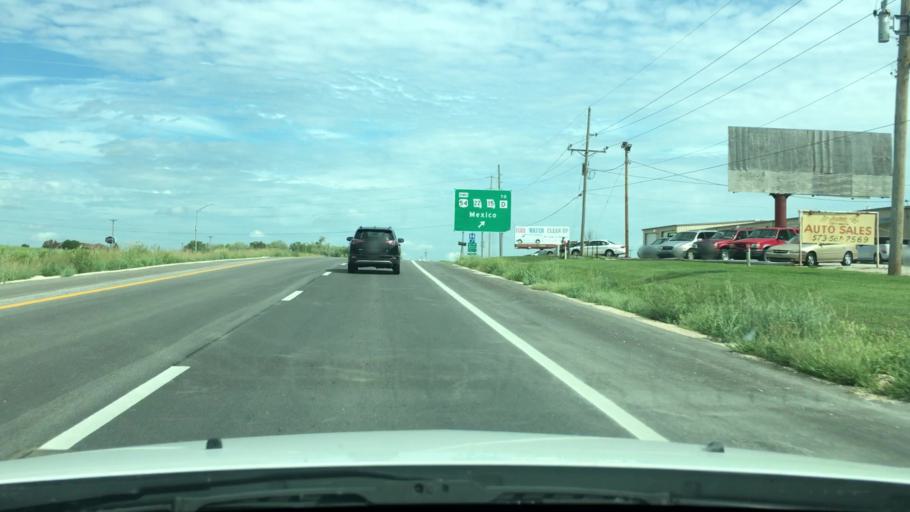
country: US
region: Missouri
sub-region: Audrain County
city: Mexico
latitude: 39.1119
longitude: -91.8951
